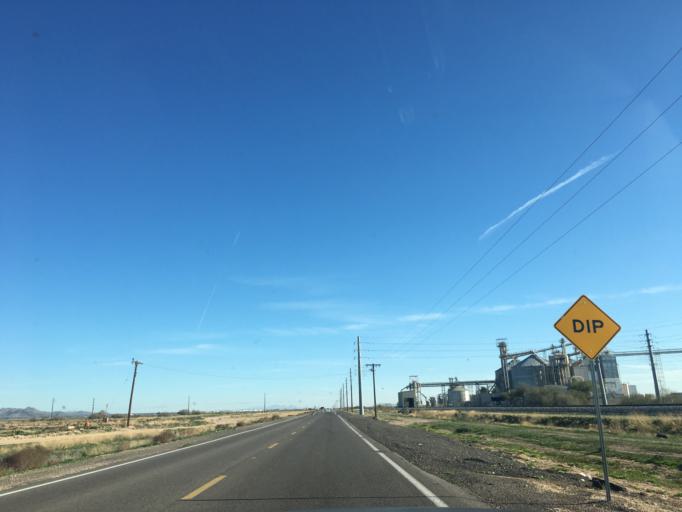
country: US
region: Arizona
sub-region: Pinal County
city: Maricopa
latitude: 33.0165
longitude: -111.9829
